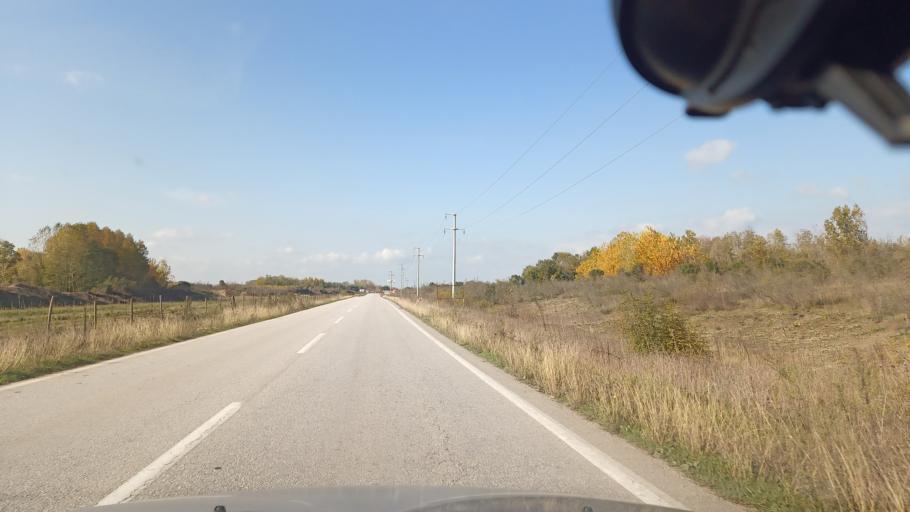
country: TR
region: Sakarya
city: Karasu
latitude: 41.1215
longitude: 30.5793
